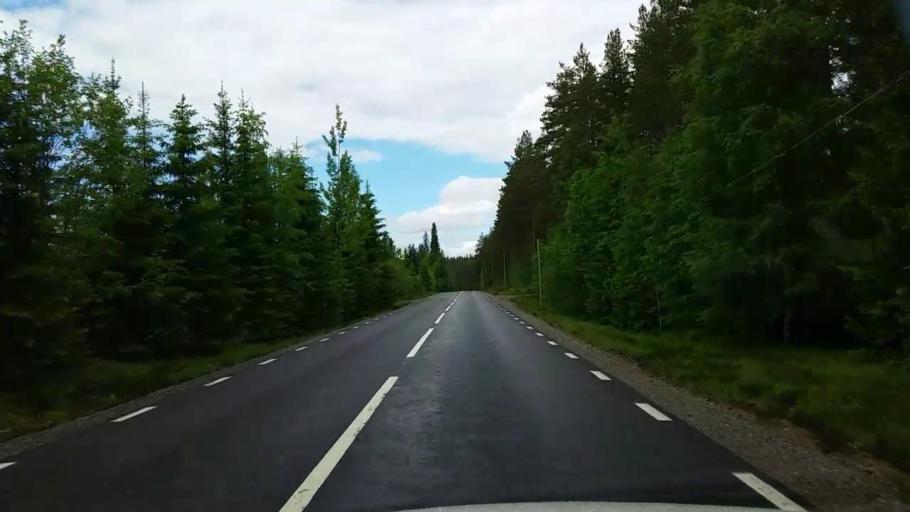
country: SE
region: Gaevleborg
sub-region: Sandvikens Kommun
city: Jarbo
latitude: 60.8600
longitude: 16.4362
